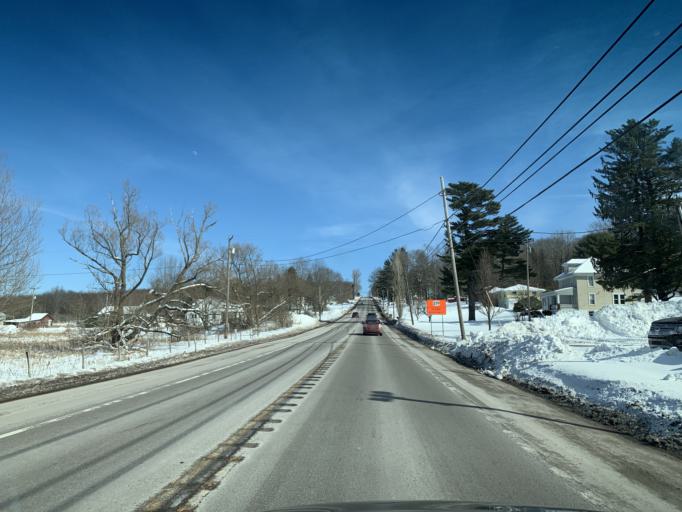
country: US
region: Pennsylvania
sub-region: Somerset County
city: Meyersdale
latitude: 39.6953
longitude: -79.1152
